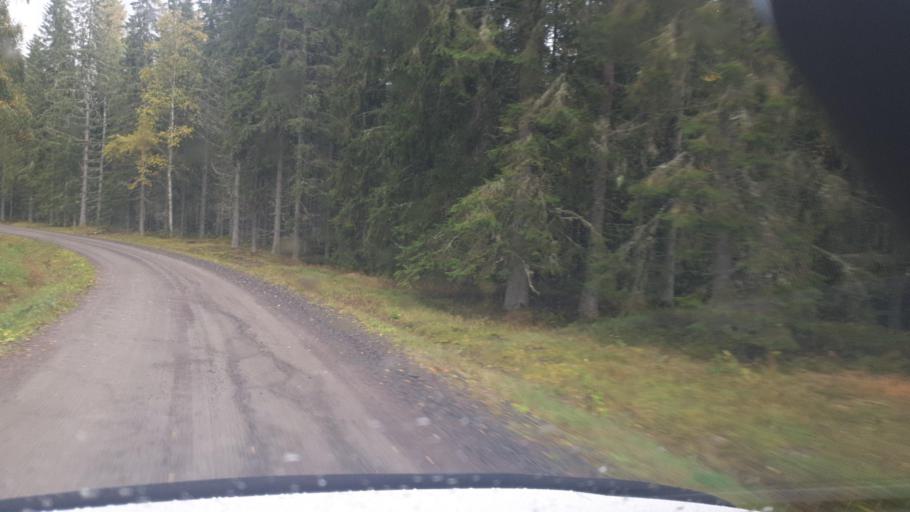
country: SE
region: Vaermland
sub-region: Sunne Kommun
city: Sunne
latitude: 59.8582
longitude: 12.8854
